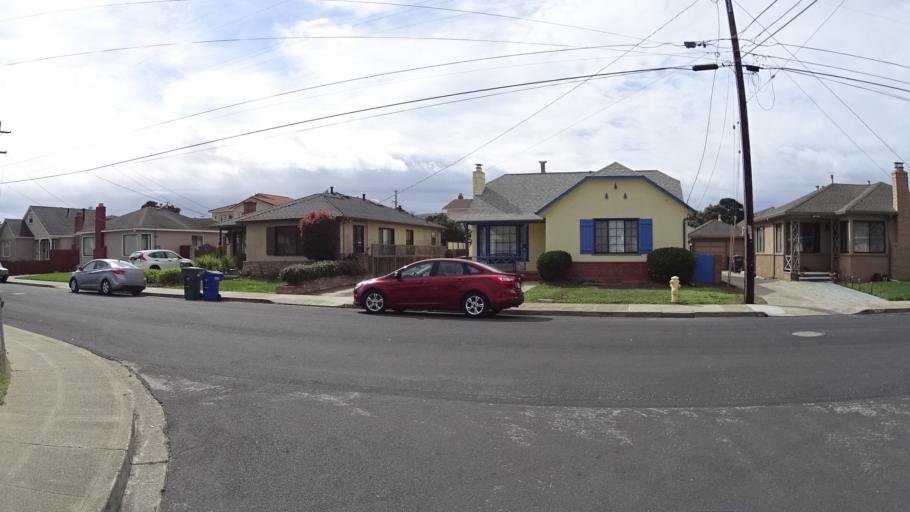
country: US
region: California
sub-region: San Mateo County
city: South San Francisco
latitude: 37.6515
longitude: -122.4246
